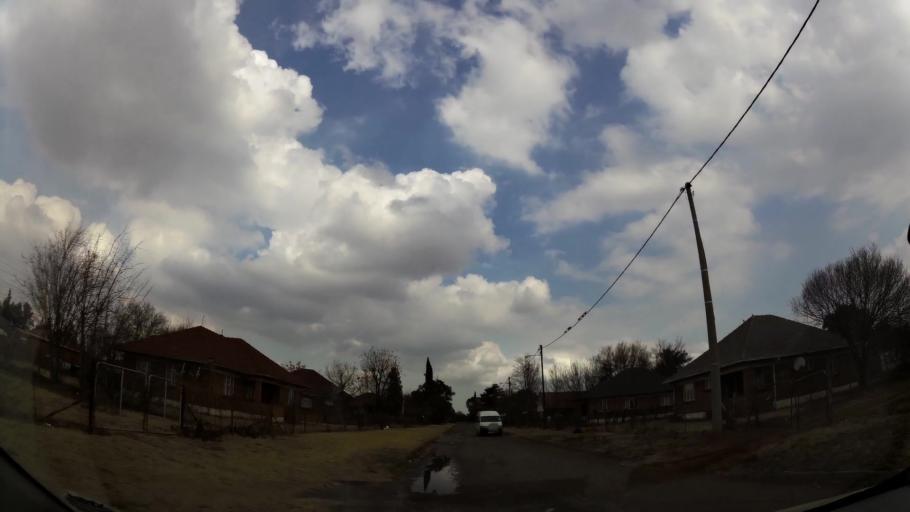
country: ZA
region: Gauteng
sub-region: Sedibeng District Municipality
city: Vereeniging
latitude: -26.6734
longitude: 27.9372
